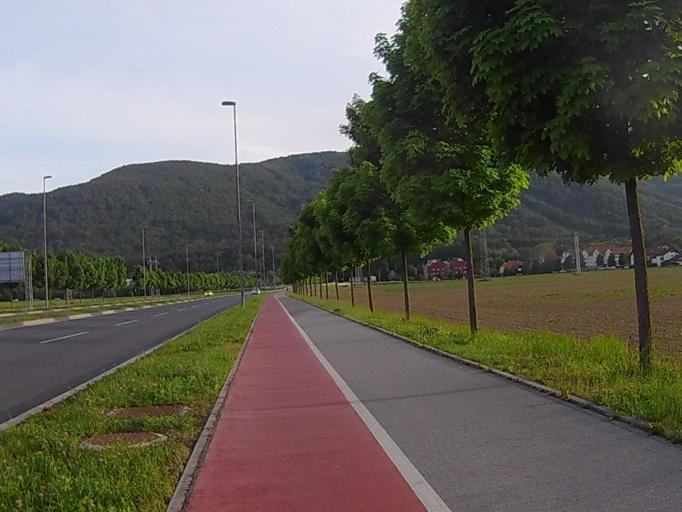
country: SI
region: Maribor
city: Pekre
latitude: 46.5417
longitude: 15.6176
